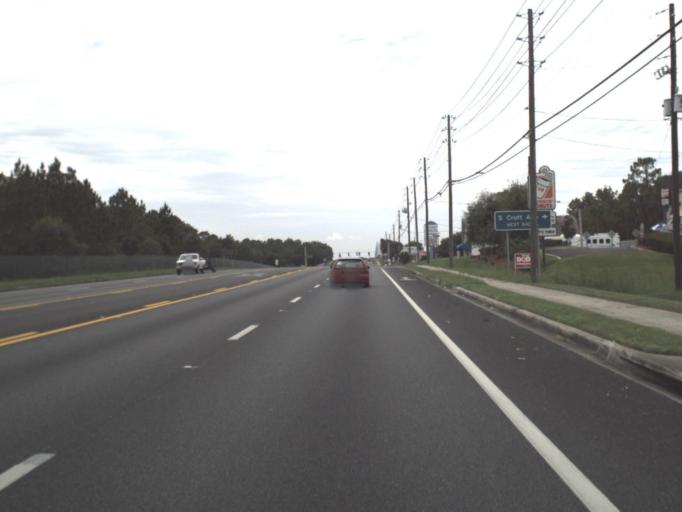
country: US
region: Florida
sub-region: Citrus County
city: Inverness Highlands North
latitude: 28.8521
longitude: -82.3825
